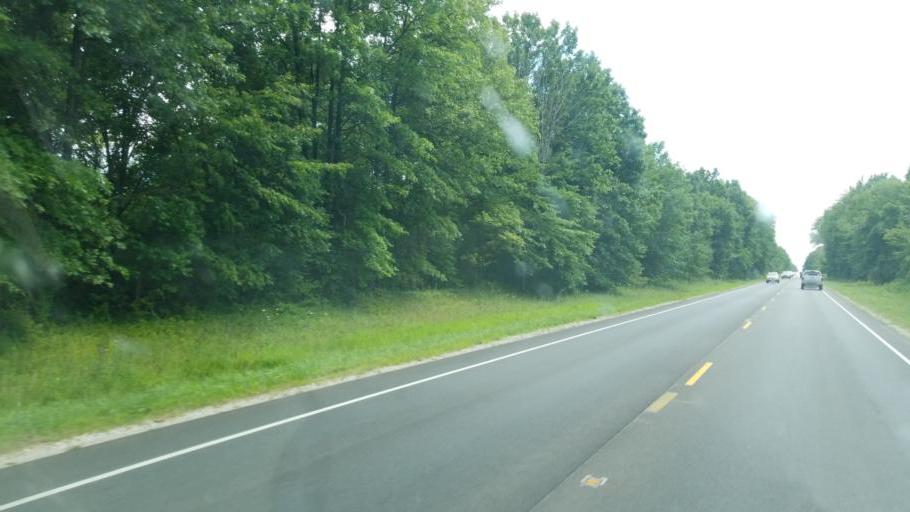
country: US
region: Ohio
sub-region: Franklin County
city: Westerville
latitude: 40.1900
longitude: -82.9099
